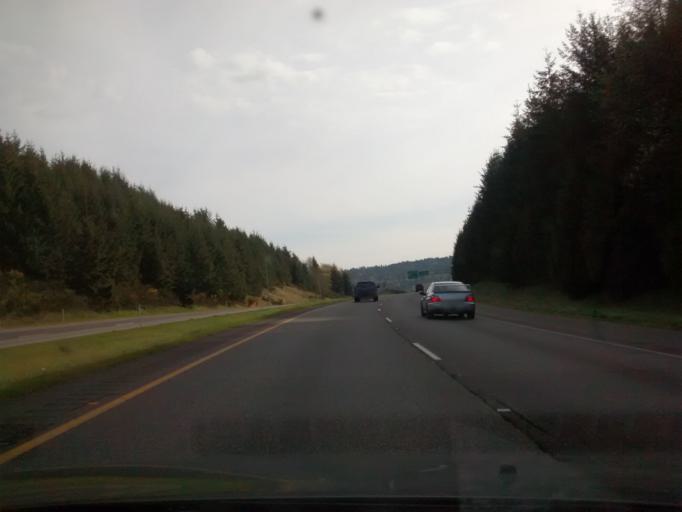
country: US
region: Washington
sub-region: Kitsap County
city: Silverdale
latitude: 47.6593
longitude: -122.7018
